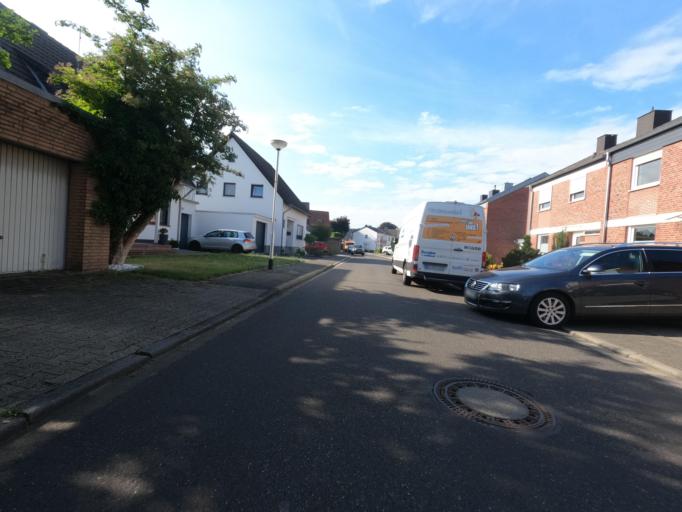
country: DE
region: North Rhine-Westphalia
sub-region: Regierungsbezirk Koln
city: Wassenberg
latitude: 51.0610
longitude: 6.1501
